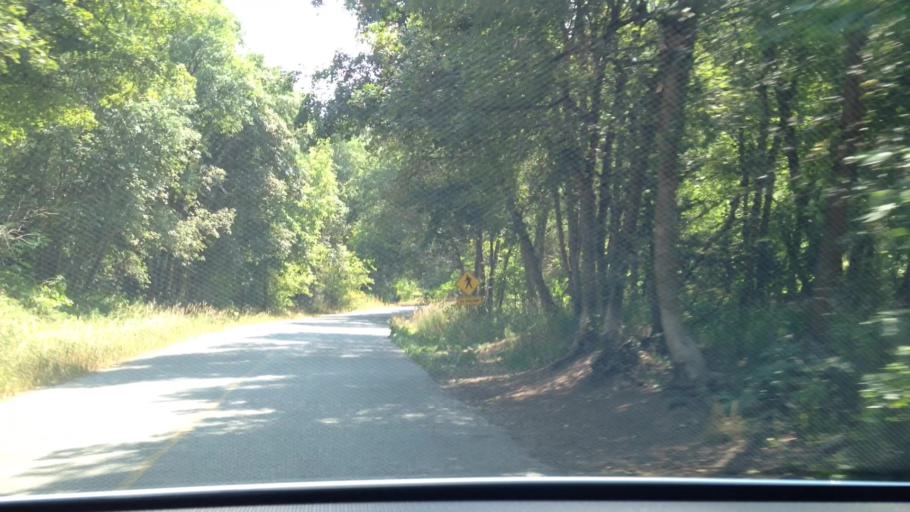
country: US
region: Utah
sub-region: Salt Lake County
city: Mount Olympus
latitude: 40.7000
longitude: -111.7123
